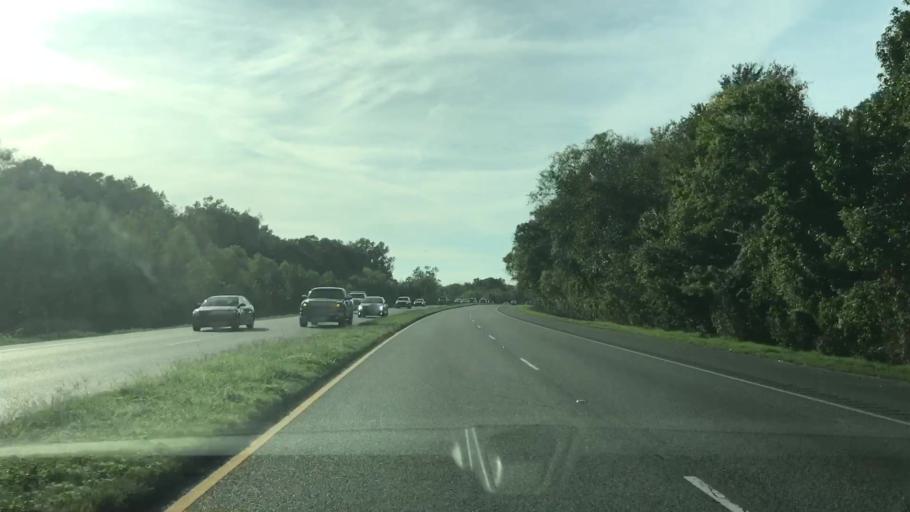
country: US
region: Louisiana
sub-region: Jefferson Parish
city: Avondale
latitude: 29.9093
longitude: -90.1859
